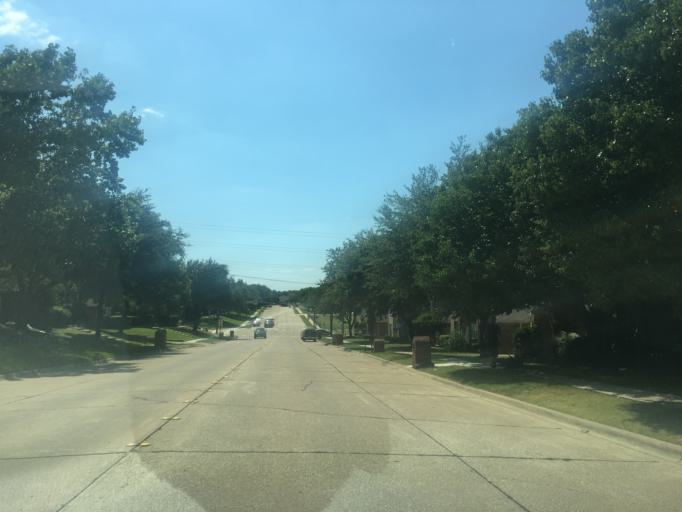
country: US
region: Texas
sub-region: Denton County
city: Lewisville
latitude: 33.0134
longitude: -97.0035
